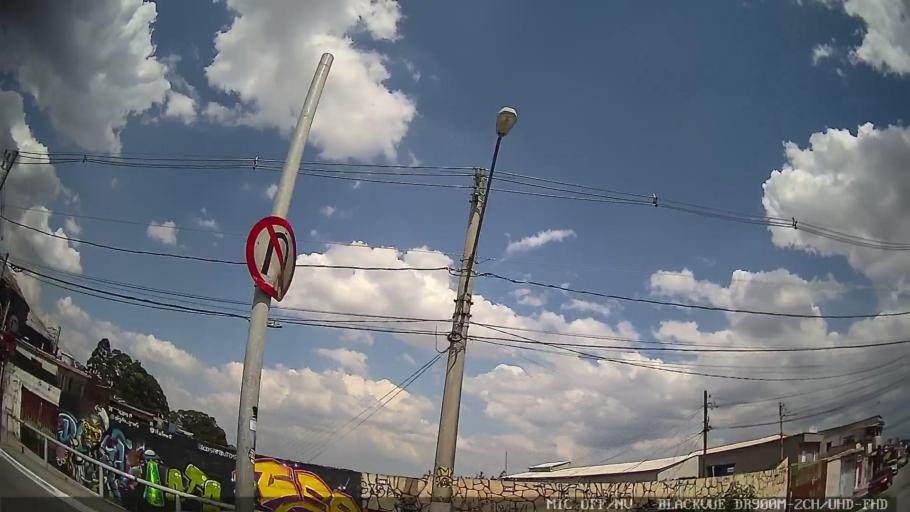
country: BR
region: Sao Paulo
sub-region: Sao Caetano Do Sul
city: Sao Caetano do Sul
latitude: -23.5514
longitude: -46.4786
